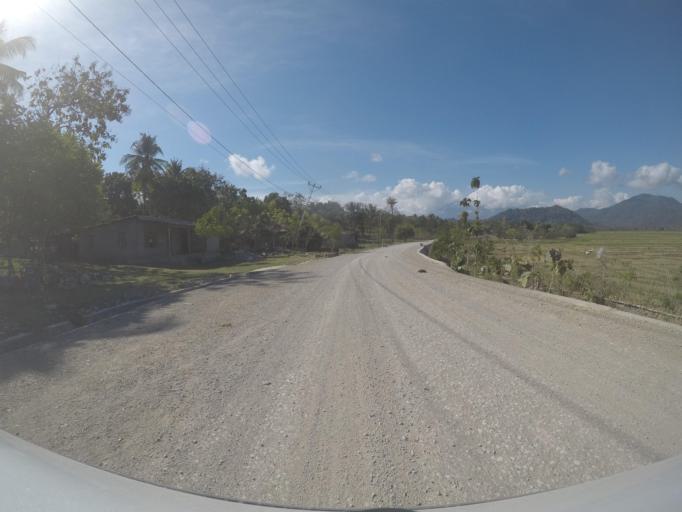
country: TL
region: Viqueque
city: Viqueque
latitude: -8.8187
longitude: 126.5333
